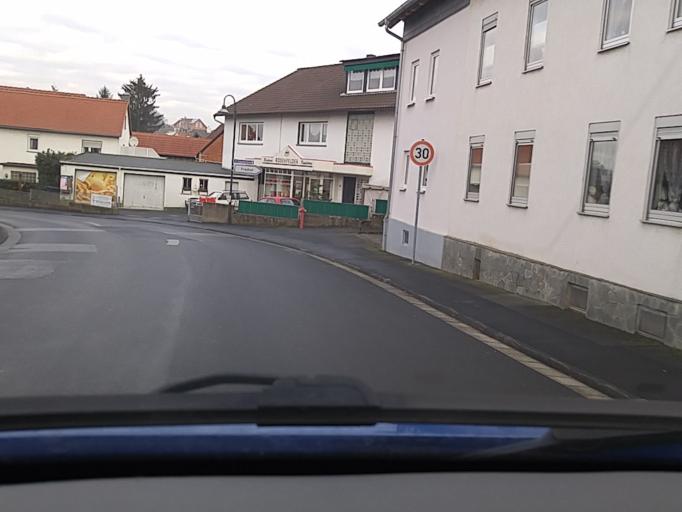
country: DE
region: Hesse
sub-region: Regierungsbezirk Darmstadt
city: Bad Nauheim
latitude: 50.3753
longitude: 8.7649
